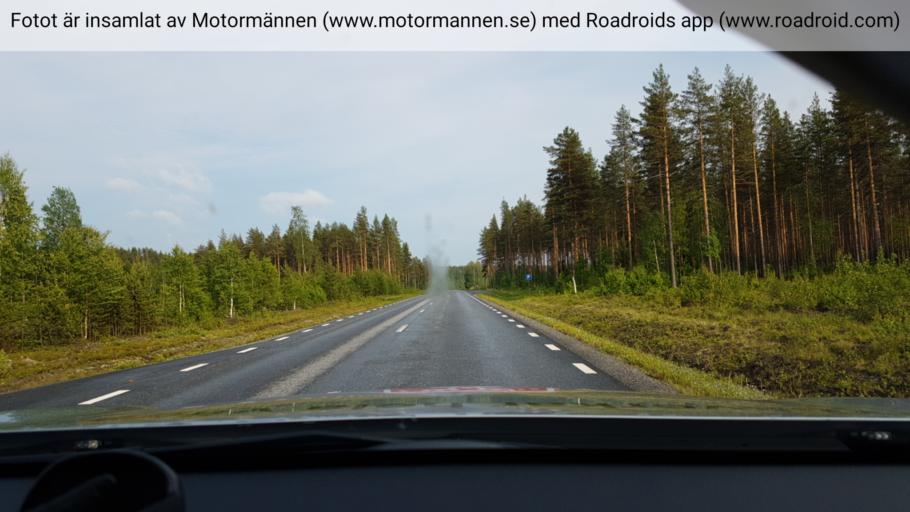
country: SE
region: Vaesterbotten
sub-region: Bjurholms Kommun
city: Bjurholm
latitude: 64.3843
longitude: 19.1151
